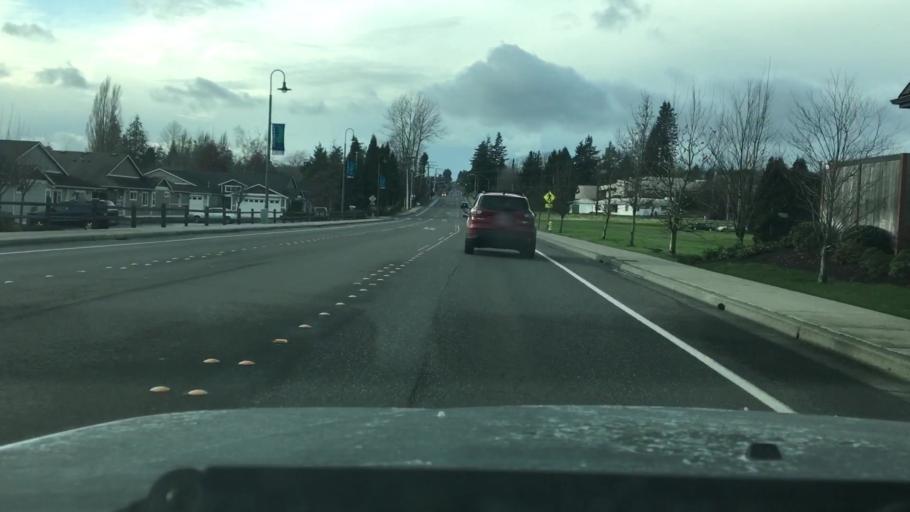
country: US
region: Washington
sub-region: Whatcom County
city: Ferndale
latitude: 48.8484
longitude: -122.5987
